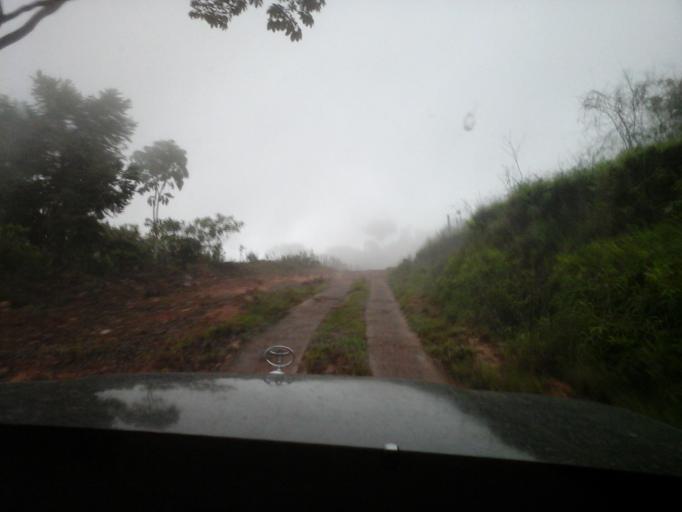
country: CO
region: Cesar
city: Agustin Codazzi
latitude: 9.9396
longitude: -73.1477
